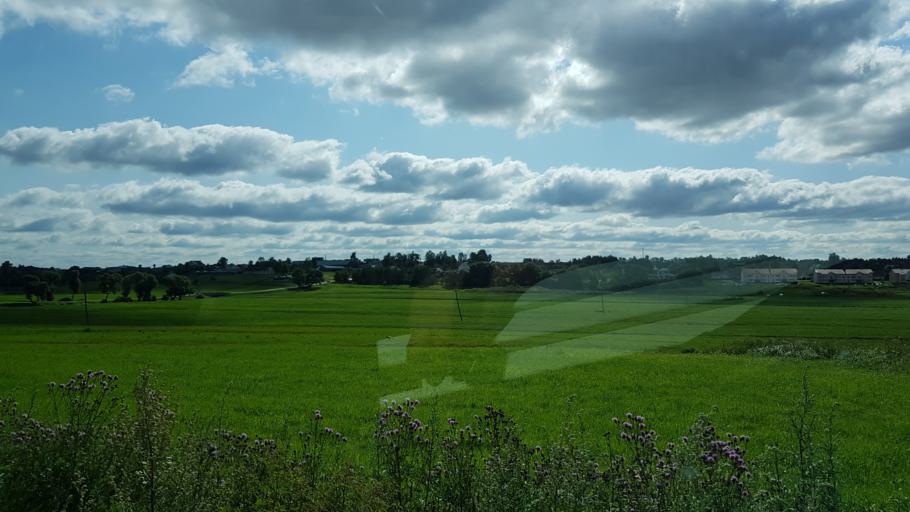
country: BY
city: Fanipol
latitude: 53.7672
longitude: 27.3205
